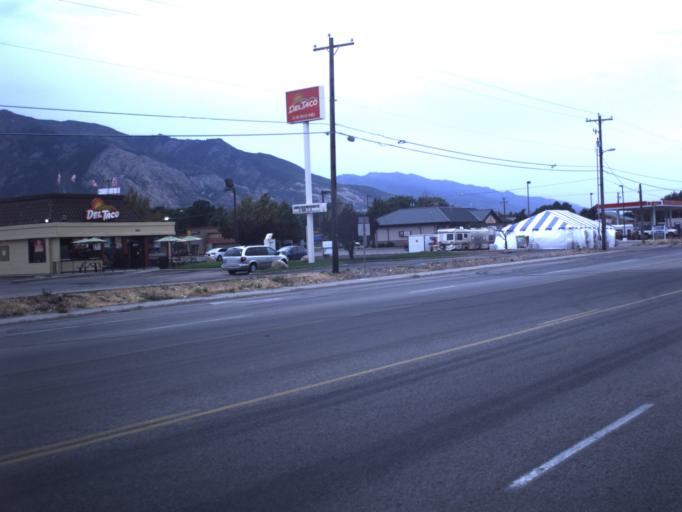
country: US
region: Utah
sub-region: Weber County
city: Ogden
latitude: 41.2463
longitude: -111.9783
